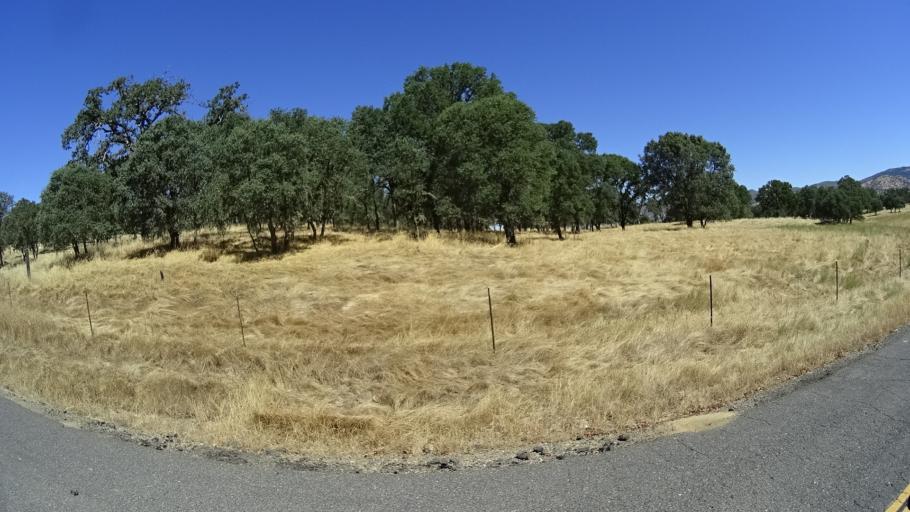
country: US
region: California
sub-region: Calaveras County
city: Copperopolis
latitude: 38.0264
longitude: -120.7268
